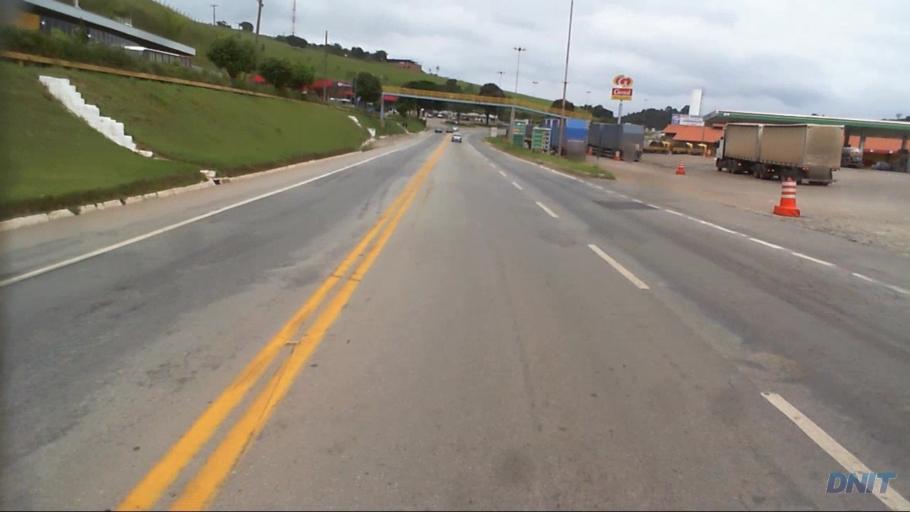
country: BR
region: Minas Gerais
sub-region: Joao Monlevade
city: Joao Monlevade
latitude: -19.8396
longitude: -43.1965
